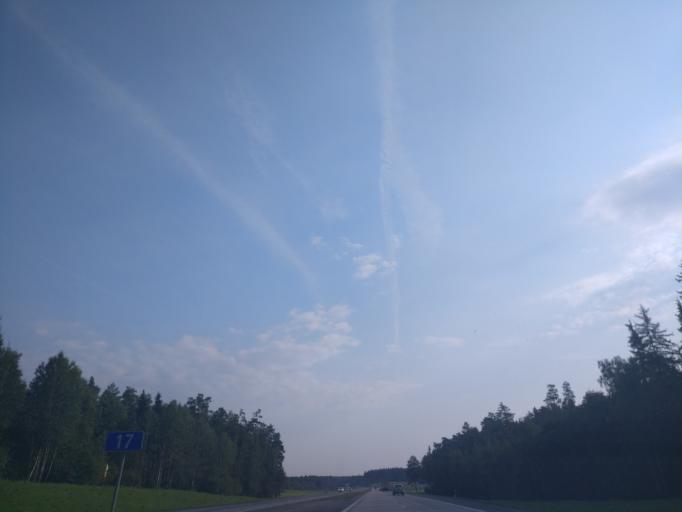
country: BY
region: Minsk
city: Borovlyany
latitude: 54.0305
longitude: 27.6794
